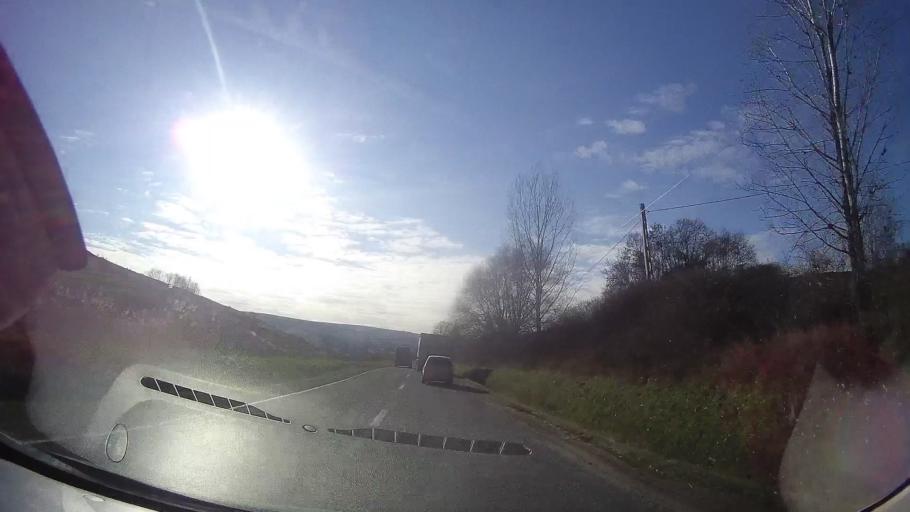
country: RO
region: Cluj
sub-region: Comuna Caianu
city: Vaida-Camaras
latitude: 46.8033
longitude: 23.9584
